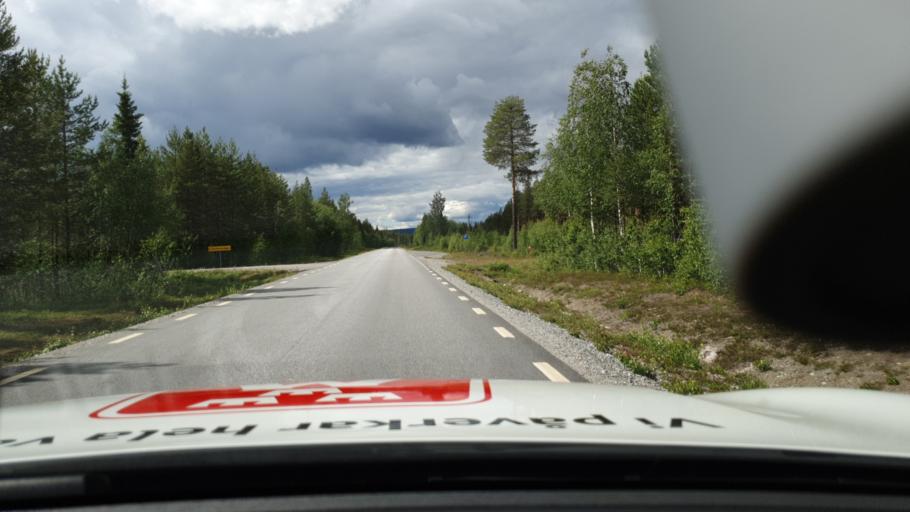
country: SE
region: Norrbotten
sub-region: Jokkmokks Kommun
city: Jokkmokk
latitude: 66.8216
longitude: 19.1754
